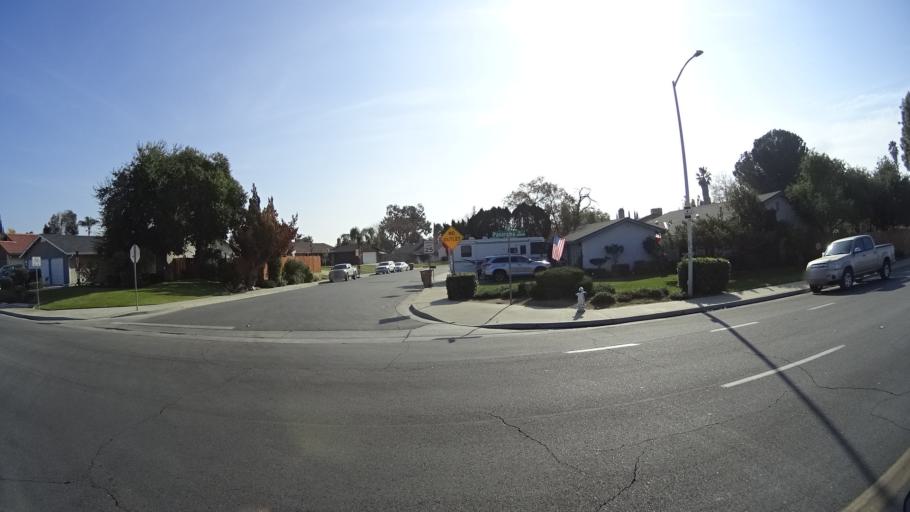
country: US
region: California
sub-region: Kern County
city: Oildale
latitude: 35.4105
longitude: -118.9441
